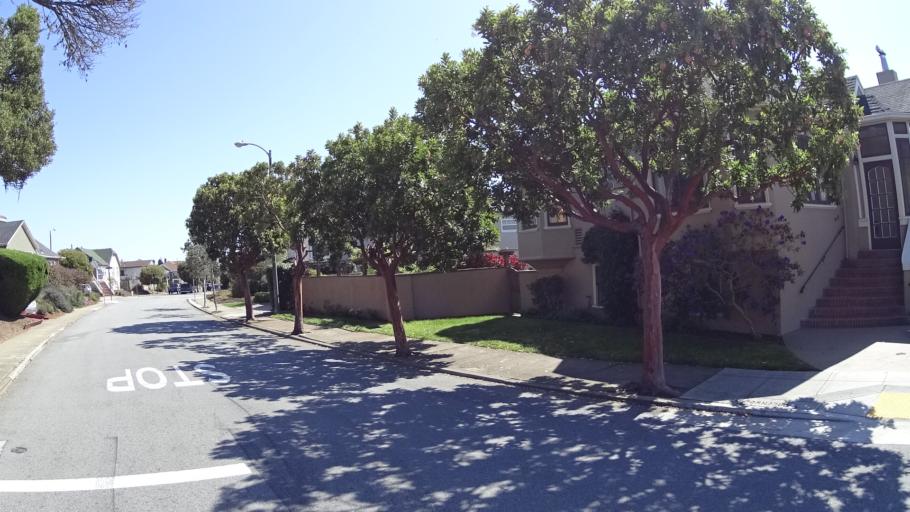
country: US
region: California
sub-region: San Mateo County
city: Daly City
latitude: 37.7288
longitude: -122.4564
